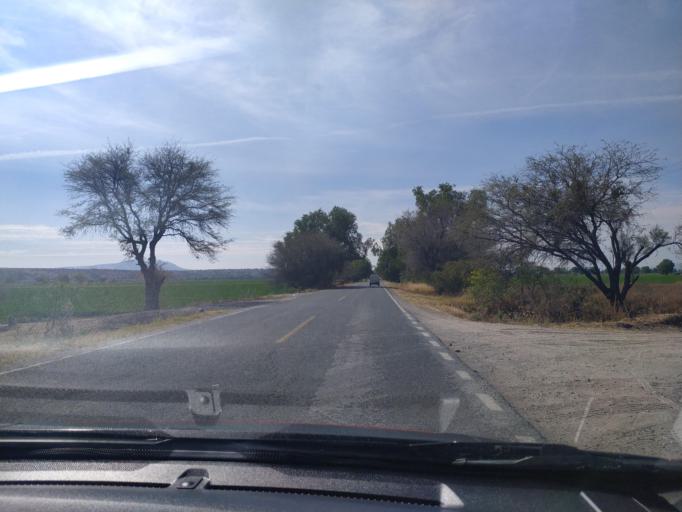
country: MX
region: Guanajuato
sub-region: San Francisco del Rincon
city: San Ignacio de Hidalgo
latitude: 20.9023
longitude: -101.8576
